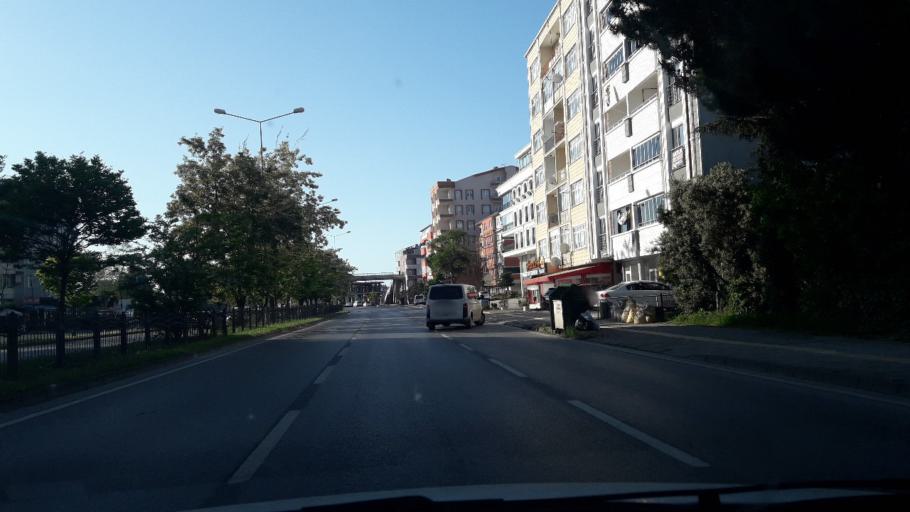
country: TR
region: Samsun
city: Taflan
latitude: 41.3704
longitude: 36.2281
